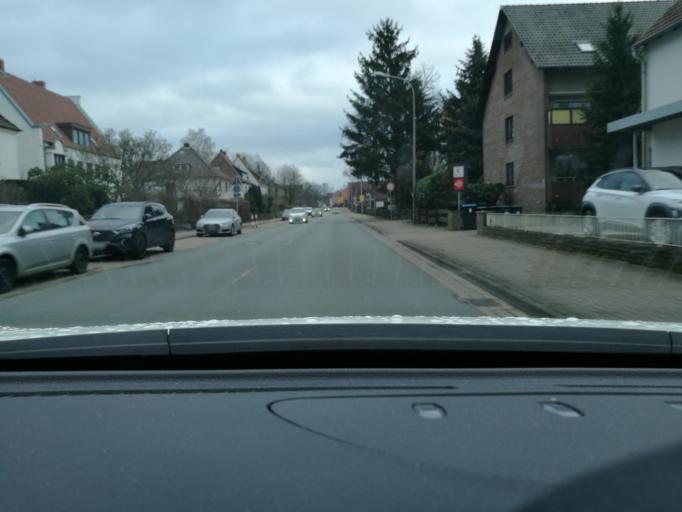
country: DE
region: Lower Saxony
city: Stadthagen
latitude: 52.3199
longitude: 9.2085
